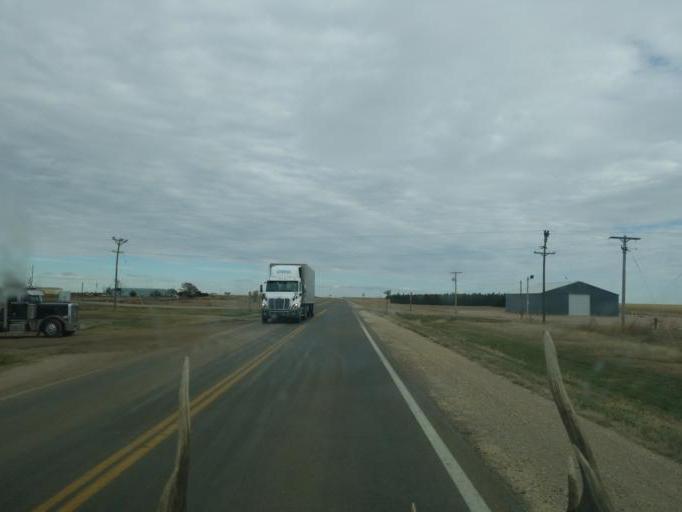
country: US
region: Kansas
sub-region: Logan County
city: Oakley
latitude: 39.0598
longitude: -101.2404
